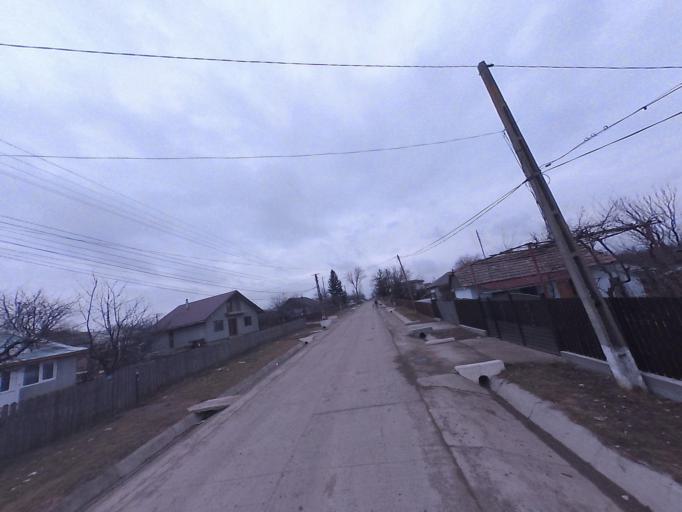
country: RO
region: Iasi
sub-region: Comuna Popricani
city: Popricani
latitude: 47.2903
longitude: 27.5069
